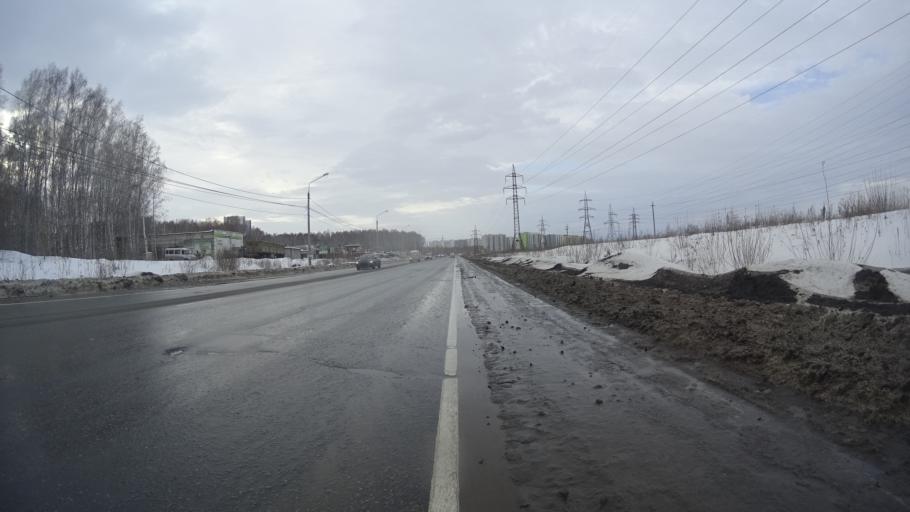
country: RU
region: Chelyabinsk
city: Roshchino
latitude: 55.2097
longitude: 61.3150
